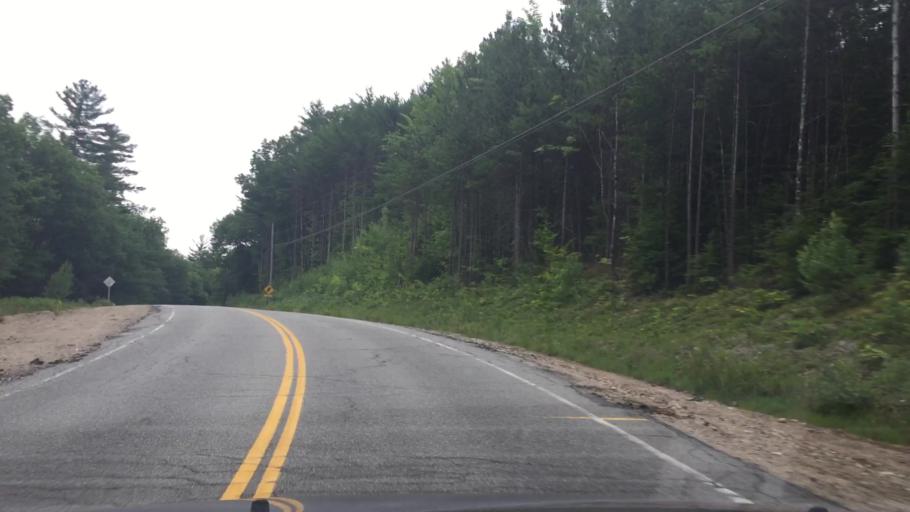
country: US
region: New Hampshire
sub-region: Carroll County
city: North Conway
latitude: 44.0839
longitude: -71.1656
